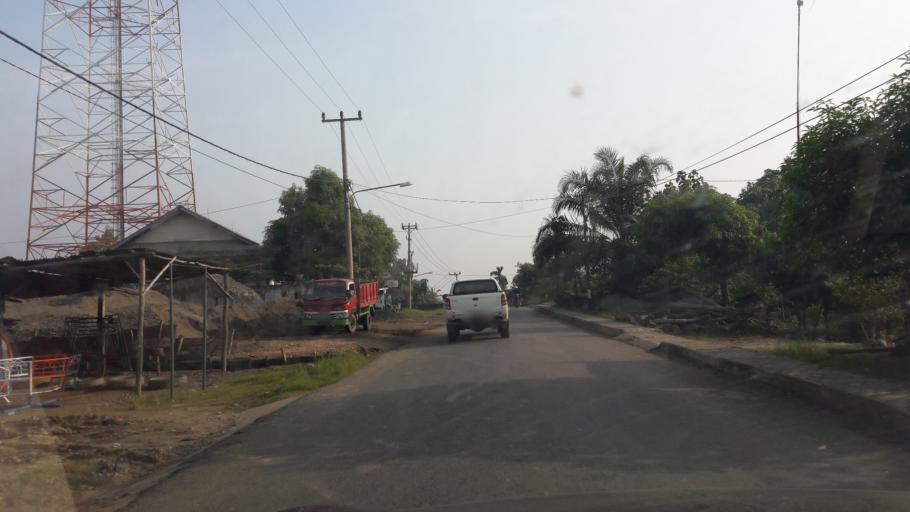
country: ID
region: South Sumatra
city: Gunungmegang Dalam
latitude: -3.2721
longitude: 103.8285
